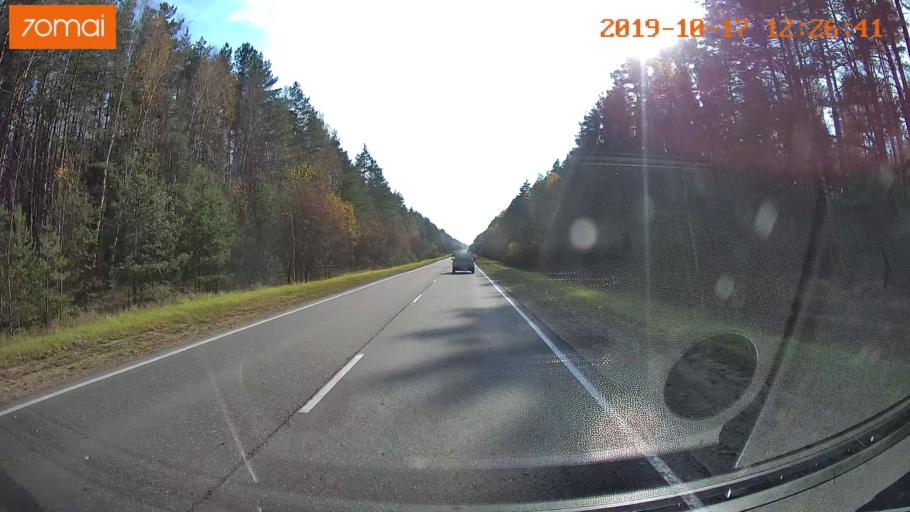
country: RU
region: Rjazan
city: Syntul
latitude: 55.0158
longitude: 41.2578
